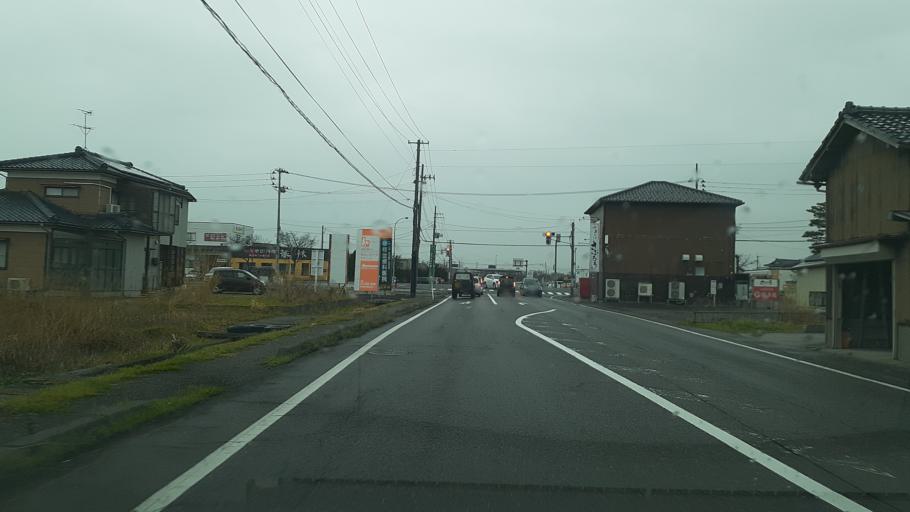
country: JP
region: Niigata
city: Kameda-honcho
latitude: 37.8803
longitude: 139.1265
